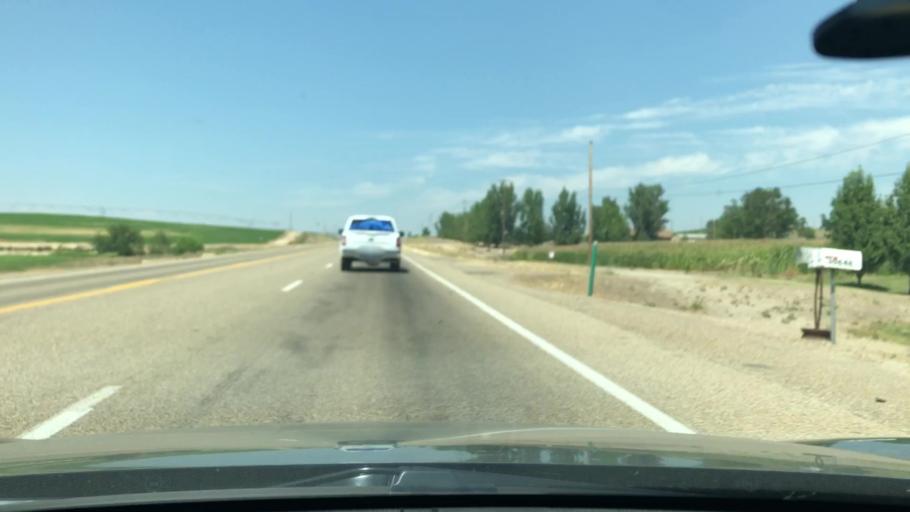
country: US
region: Idaho
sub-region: Canyon County
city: Parma
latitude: 43.8168
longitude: -116.9543
